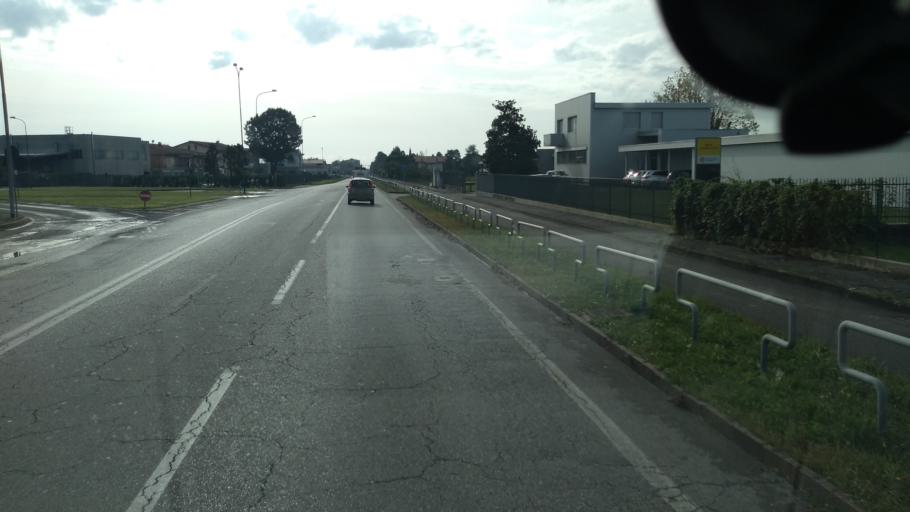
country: IT
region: Lombardy
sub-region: Provincia di Bergamo
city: Urgnano
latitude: 45.6082
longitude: 9.6958
